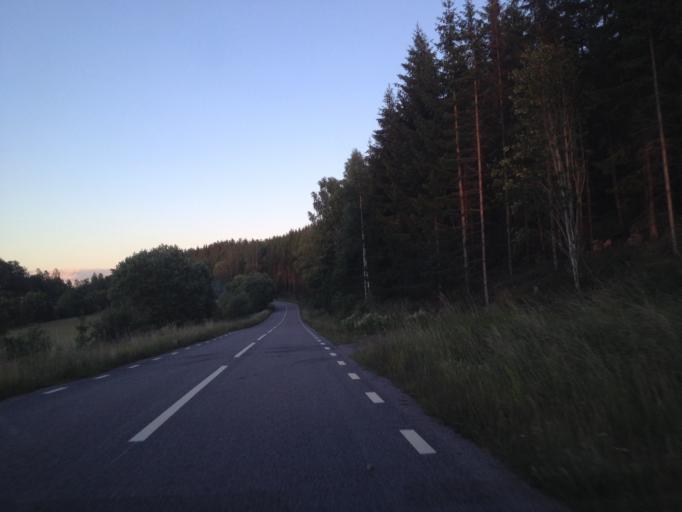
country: SE
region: Kalmar
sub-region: Vasterviks Kommun
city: Overum
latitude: 58.0187
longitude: 16.1488
